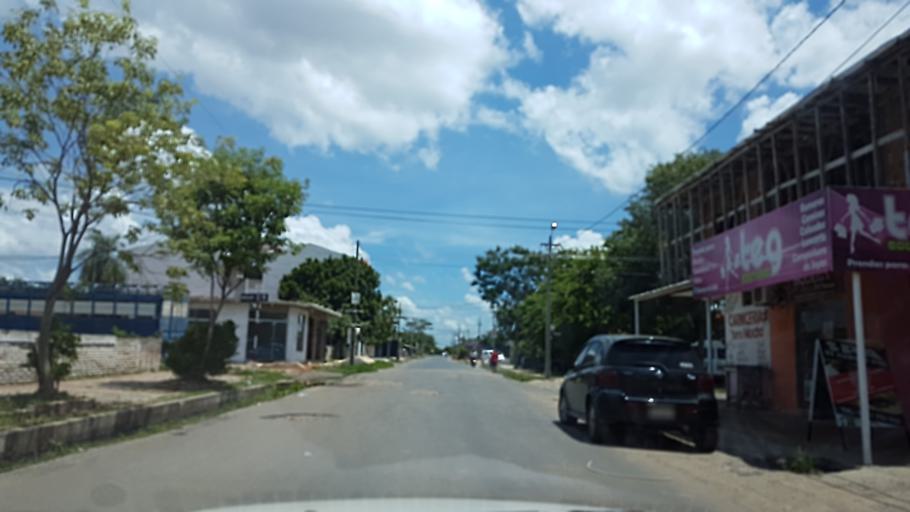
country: PY
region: Central
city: Colonia Mariano Roque Alonso
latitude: -25.2113
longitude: -57.5349
